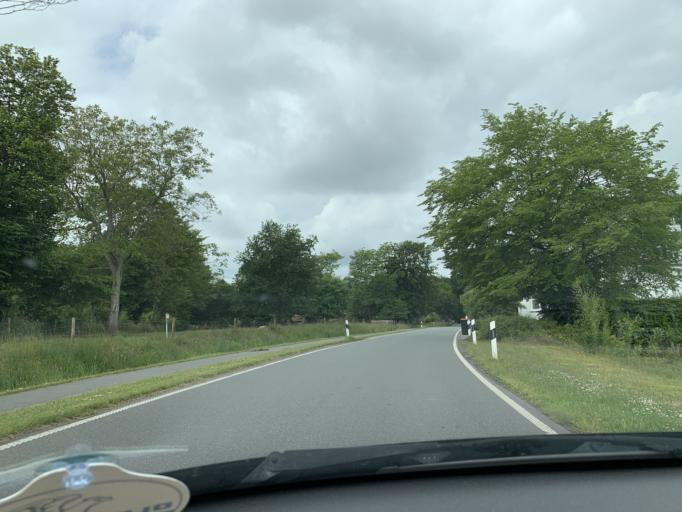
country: DE
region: Lower Saxony
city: Varel
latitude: 53.3760
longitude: 8.0848
